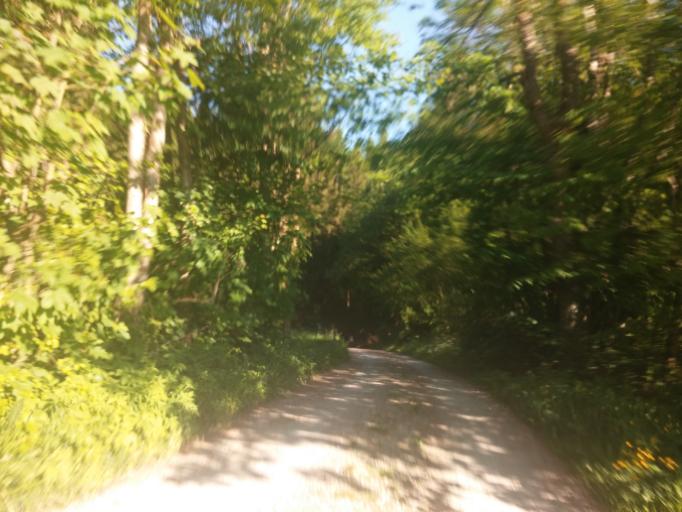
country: DE
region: Bavaria
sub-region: Swabia
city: Kronburg
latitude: 47.8738
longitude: 10.1779
